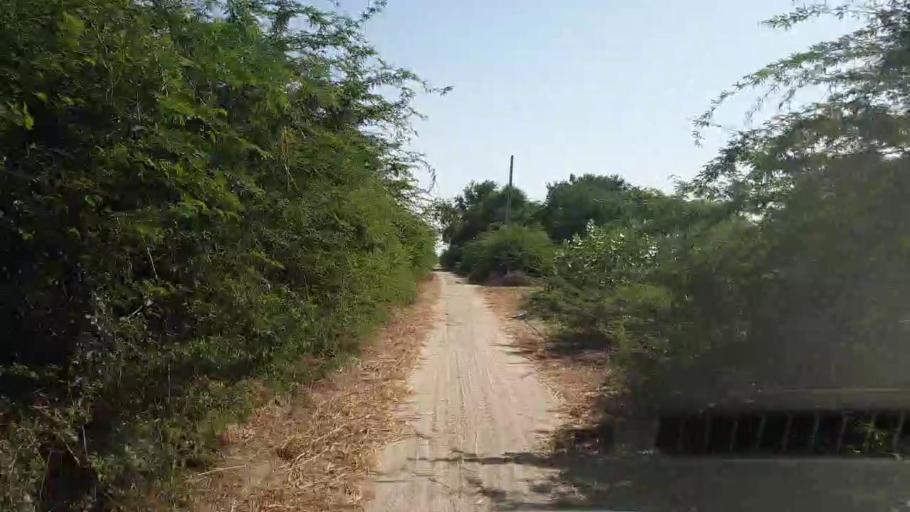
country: PK
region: Sindh
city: Tando Bago
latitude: 24.6411
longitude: 68.9892
